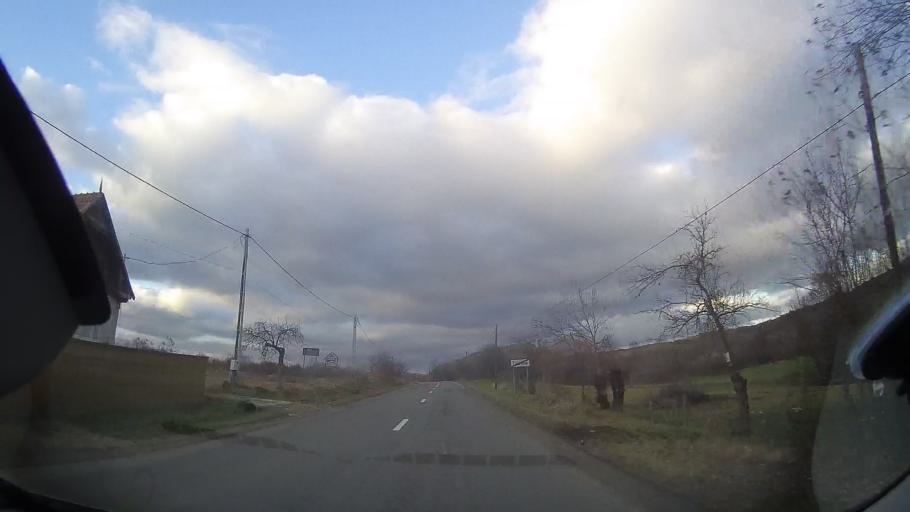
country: RO
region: Cluj
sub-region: Comuna Calatele
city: Calatele
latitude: 46.7791
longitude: 23.0060
